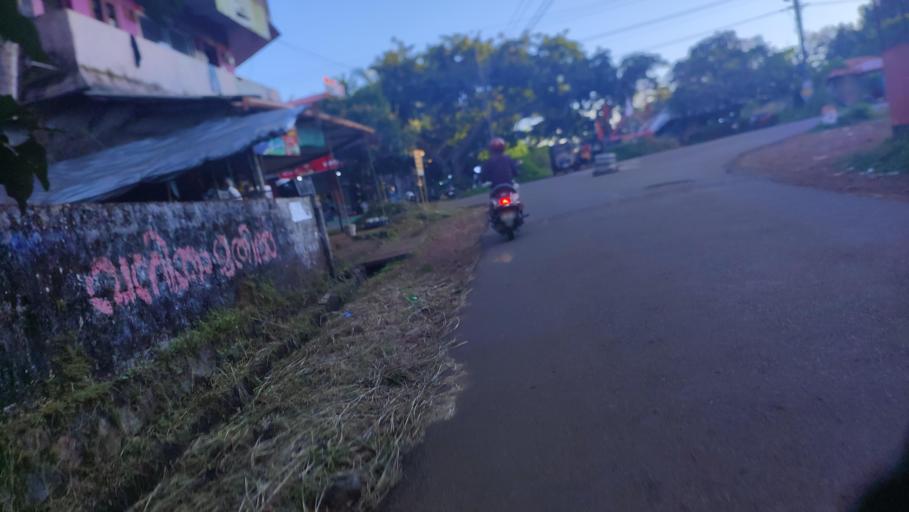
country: IN
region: Kerala
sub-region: Kasaragod District
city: Kannangad
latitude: 12.4100
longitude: 75.0949
